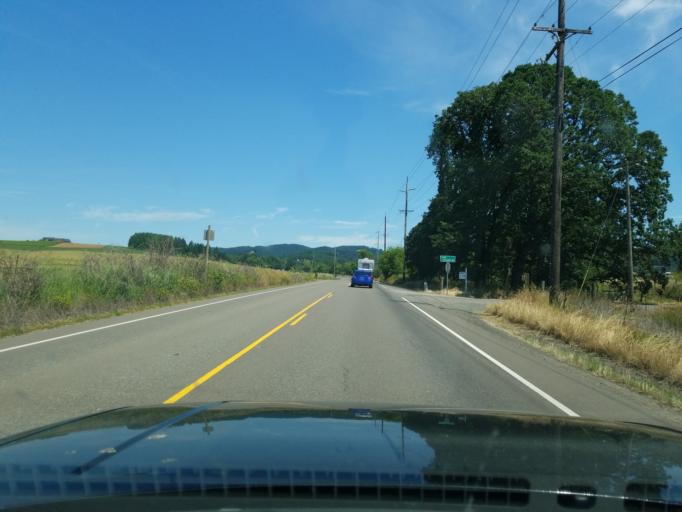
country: US
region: Oregon
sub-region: Yamhill County
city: Yamhill
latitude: 45.3557
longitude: -123.1703
